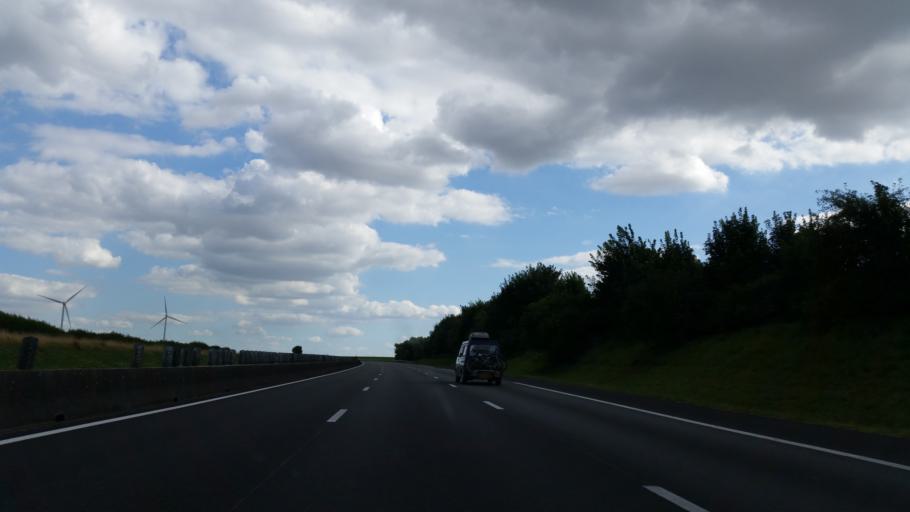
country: FR
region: Nord-Pas-de-Calais
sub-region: Departement du Pas-de-Calais
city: Bapaume
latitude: 50.0488
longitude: 2.8756
